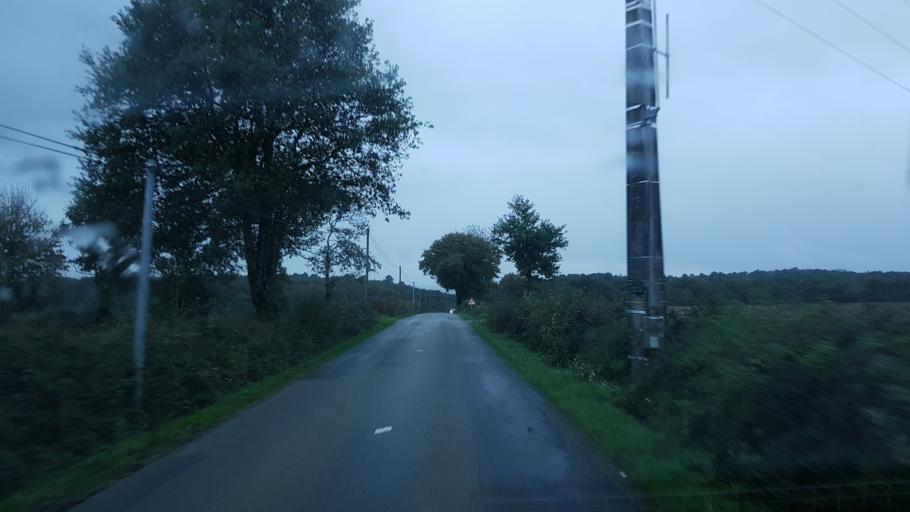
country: FR
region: Brittany
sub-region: Departement du Morbihan
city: Trefflean
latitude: 47.6736
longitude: -2.6091
